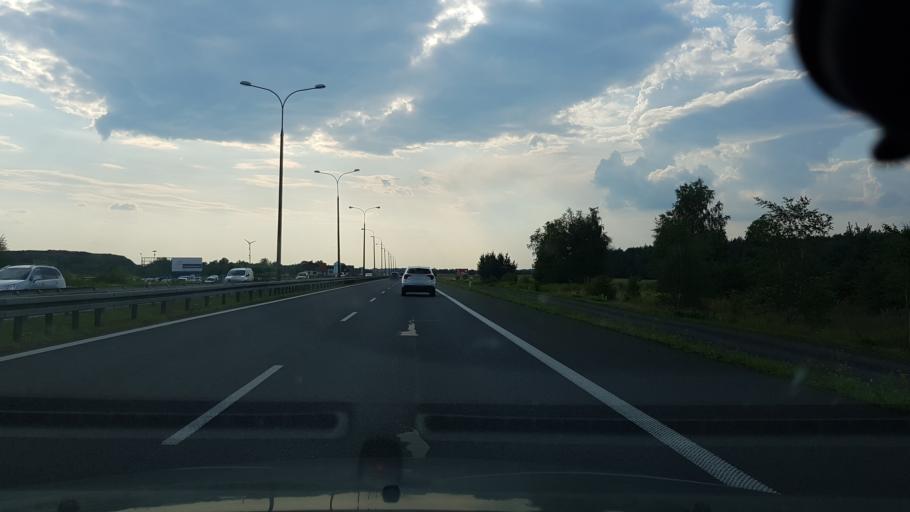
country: PL
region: Masovian Voivodeship
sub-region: Powiat nowodworski
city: Zakroczym
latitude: 52.4420
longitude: 20.6319
